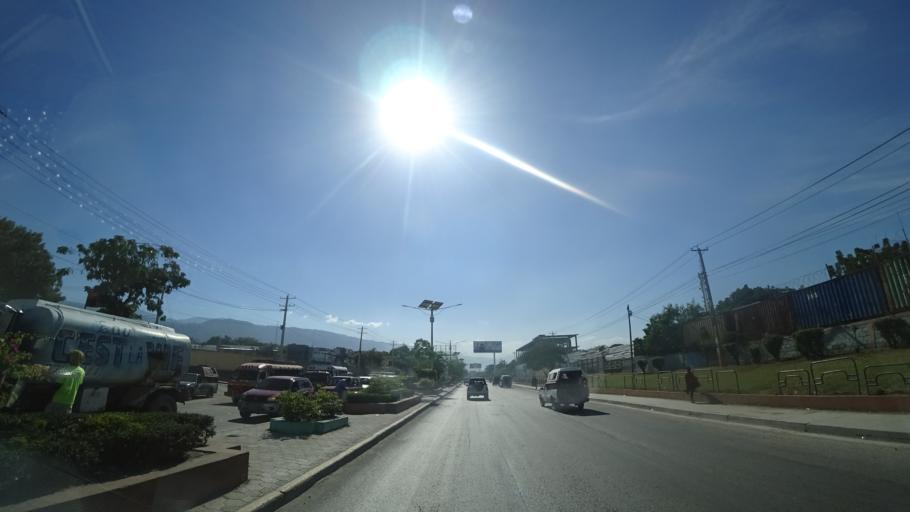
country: HT
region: Ouest
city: Delmas 73
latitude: 18.5721
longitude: -72.3072
